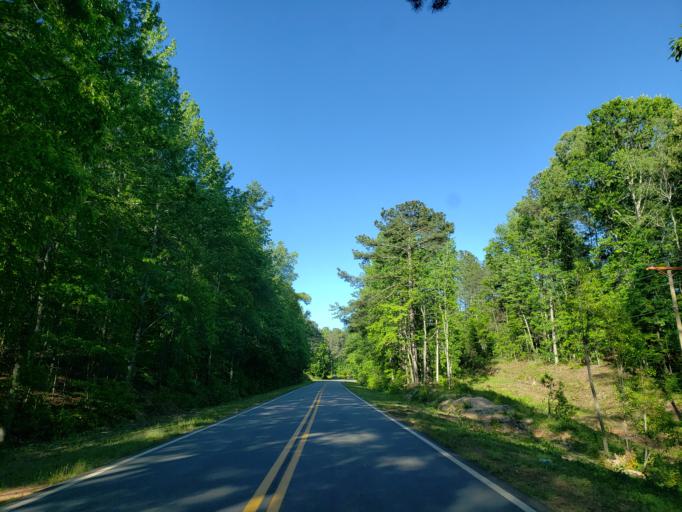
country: US
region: Georgia
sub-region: Haralson County
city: Tallapoosa
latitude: 33.7942
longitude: -85.2620
